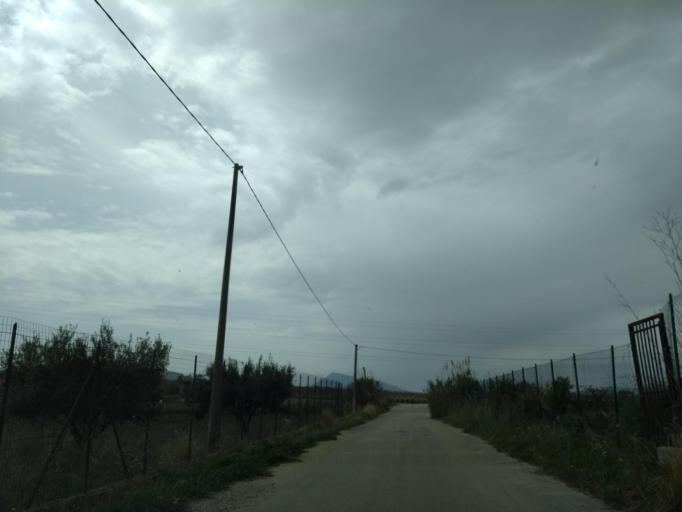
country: IT
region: Sicily
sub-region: Palermo
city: Partinico
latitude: 37.9906
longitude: 13.0692
